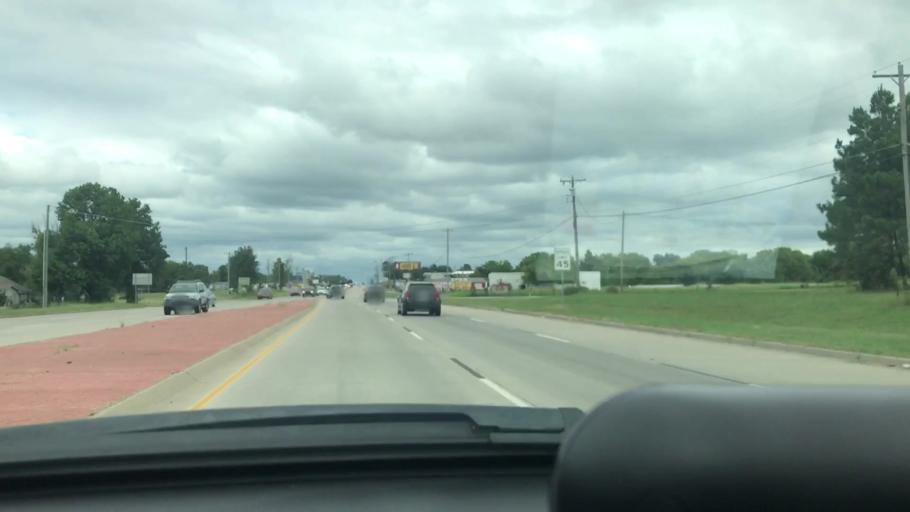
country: US
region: Oklahoma
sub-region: Muskogee County
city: Muskogee
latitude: 35.7706
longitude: -95.4024
